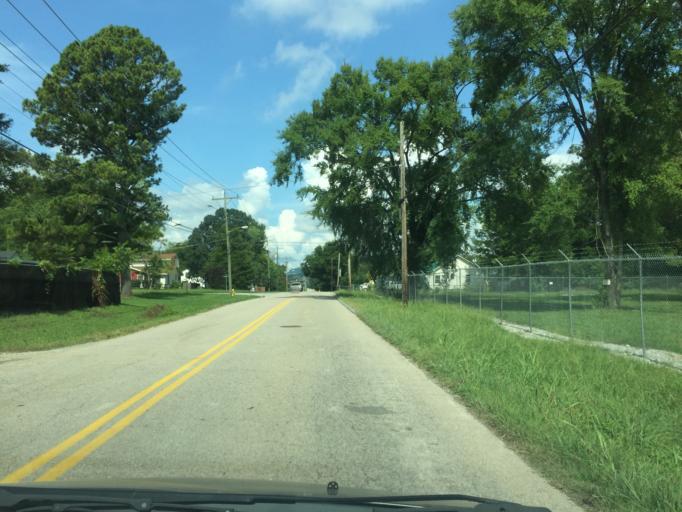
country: US
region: Tennessee
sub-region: Hamilton County
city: East Chattanooga
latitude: 35.0781
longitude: -85.2557
